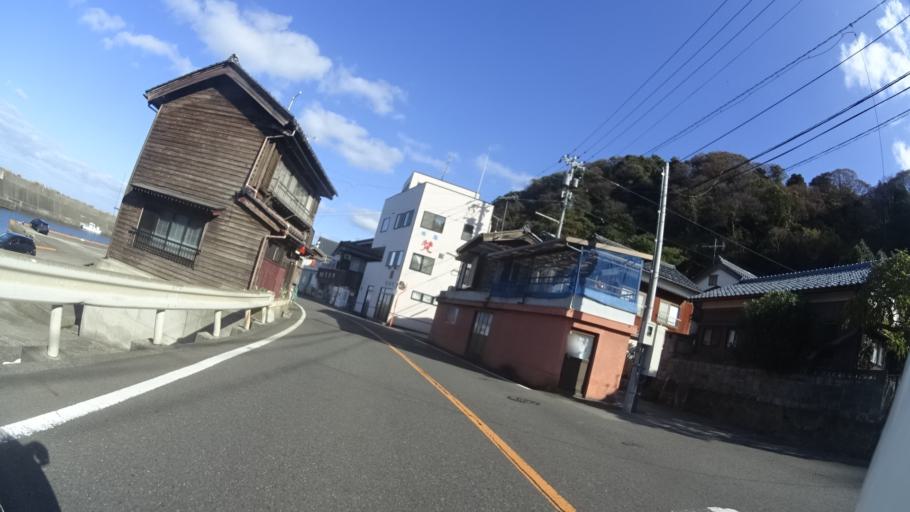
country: JP
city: Asahi
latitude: 35.8951
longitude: 135.9955
